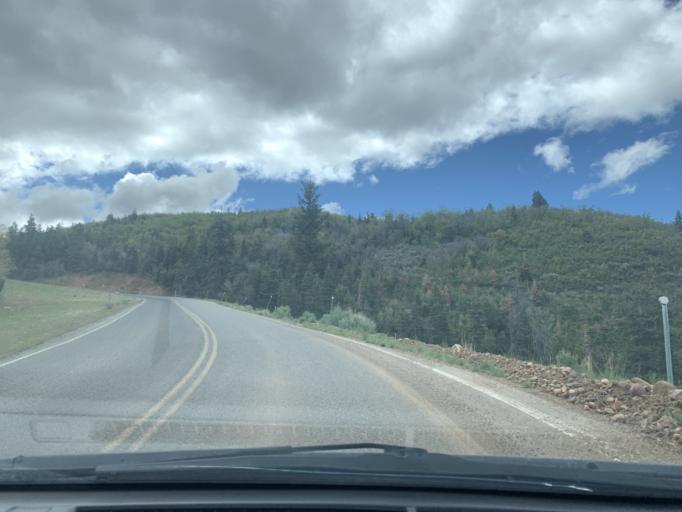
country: US
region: Utah
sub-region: Juab County
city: Nephi
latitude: 39.7805
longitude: -111.6918
